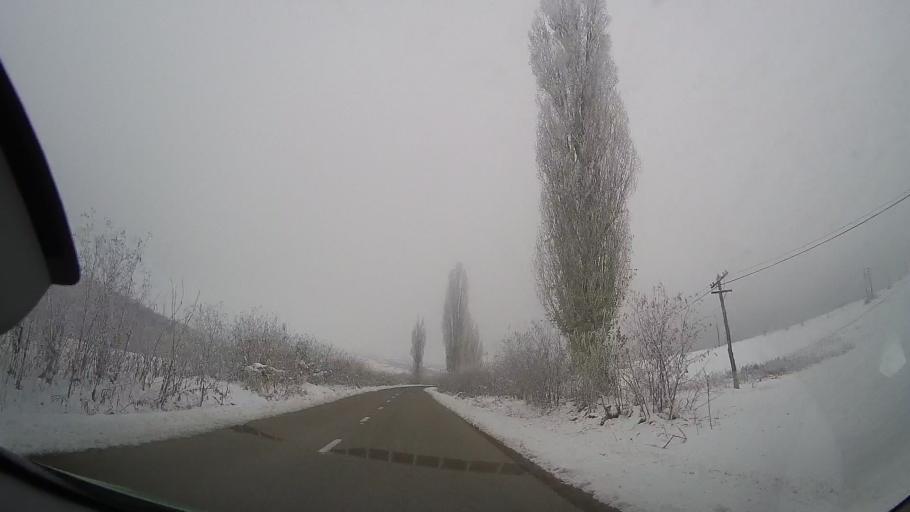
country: RO
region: Neamt
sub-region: Comuna Valea Ursului
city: Valea Ursului
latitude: 46.8027
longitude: 27.1059
